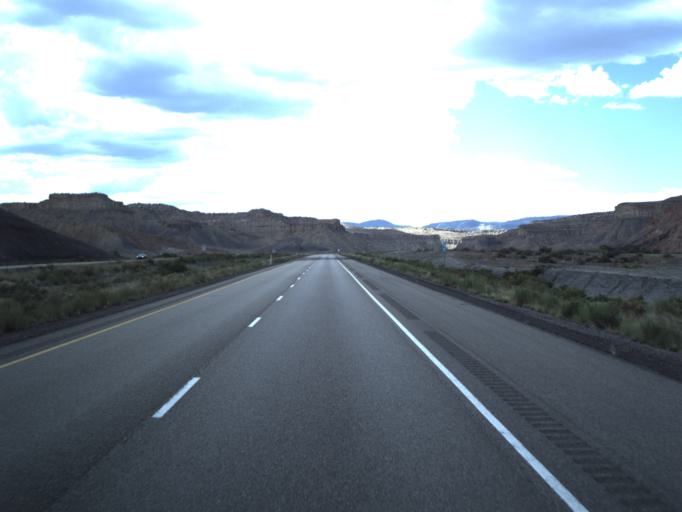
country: US
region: Utah
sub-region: Emery County
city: Ferron
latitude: 38.8108
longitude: -111.2186
